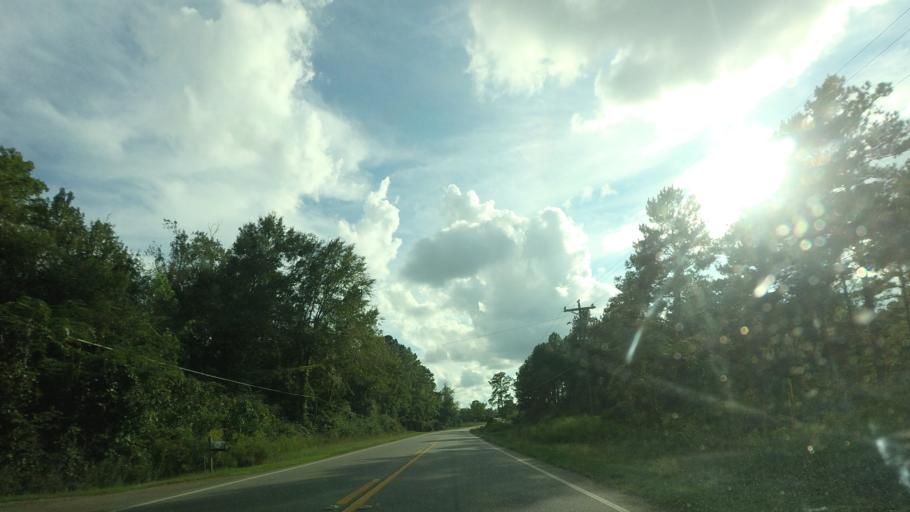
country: US
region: Georgia
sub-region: Pulaski County
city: Hawkinsville
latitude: 32.2959
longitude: -83.4322
